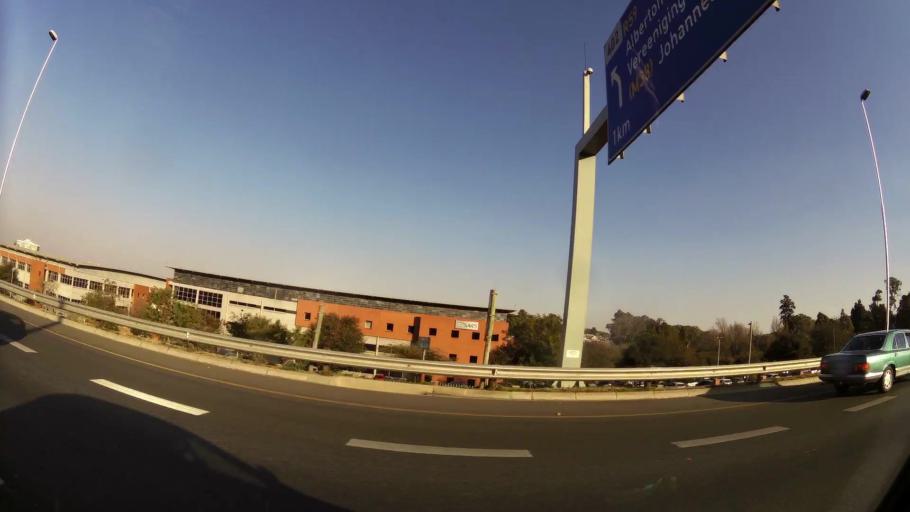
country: ZA
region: Gauteng
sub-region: Ekurhuleni Metropolitan Municipality
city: Germiston
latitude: -26.2596
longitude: 28.1125
